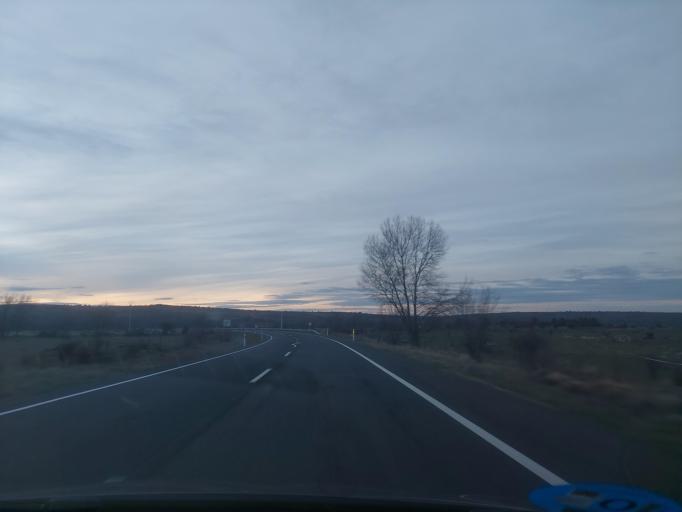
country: ES
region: Castille and Leon
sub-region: Provincia de Segovia
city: Torre Val de San Pedro
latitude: 41.0626
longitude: -3.8830
